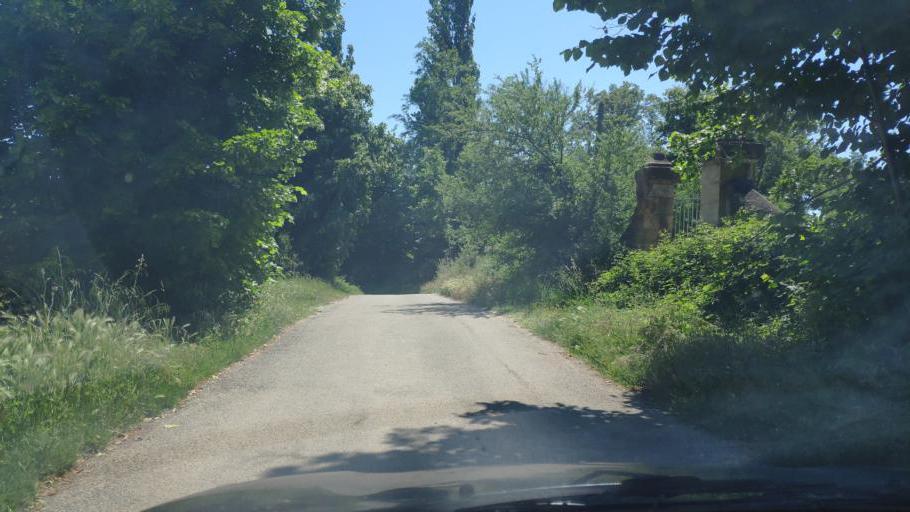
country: FR
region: Provence-Alpes-Cote d'Azur
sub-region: Departement du Vaucluse
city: Aubignan
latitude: 44.0872
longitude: 5.0566
